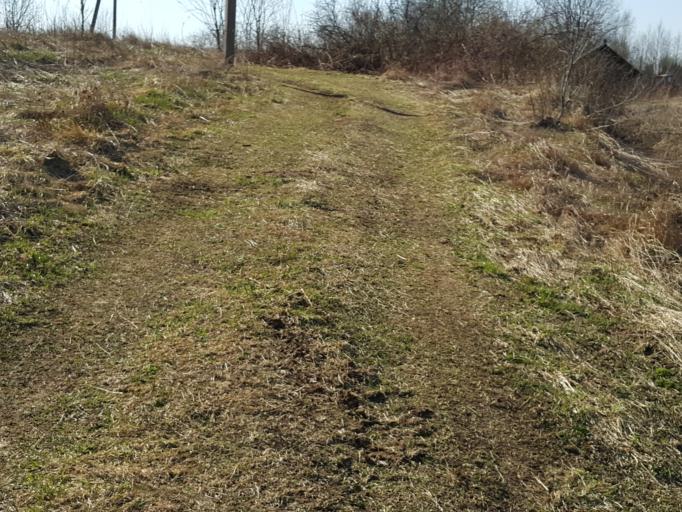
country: RU
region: Leningrad
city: Podporozh'ye
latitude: 60.3530
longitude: 34.8376
